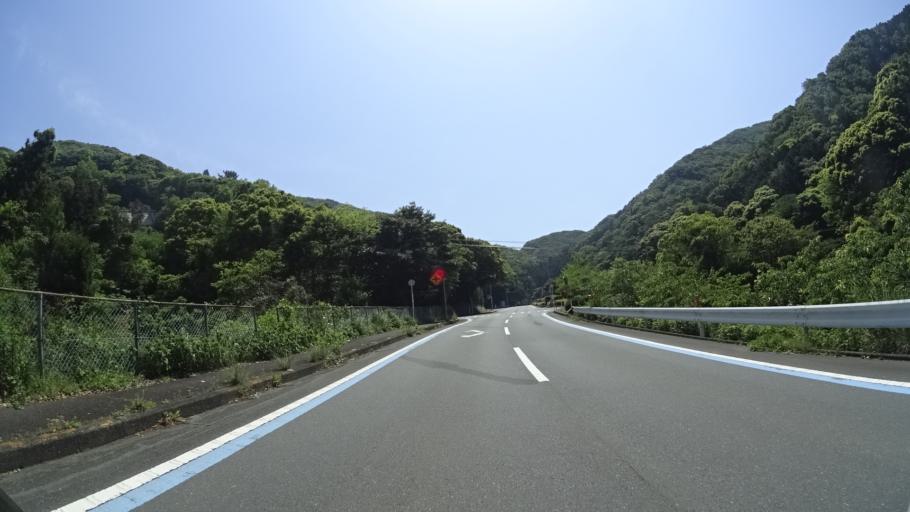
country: JP
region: Ehime
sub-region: Nishiuwa-gun
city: Ikata-cho
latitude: 33.3960
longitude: 132.1493
